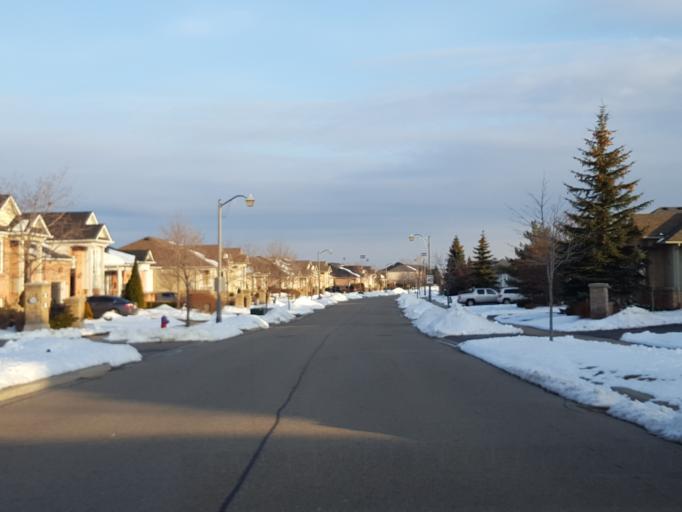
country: CA
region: Ontario
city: Burlington
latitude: 43.4017
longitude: -79.8040
